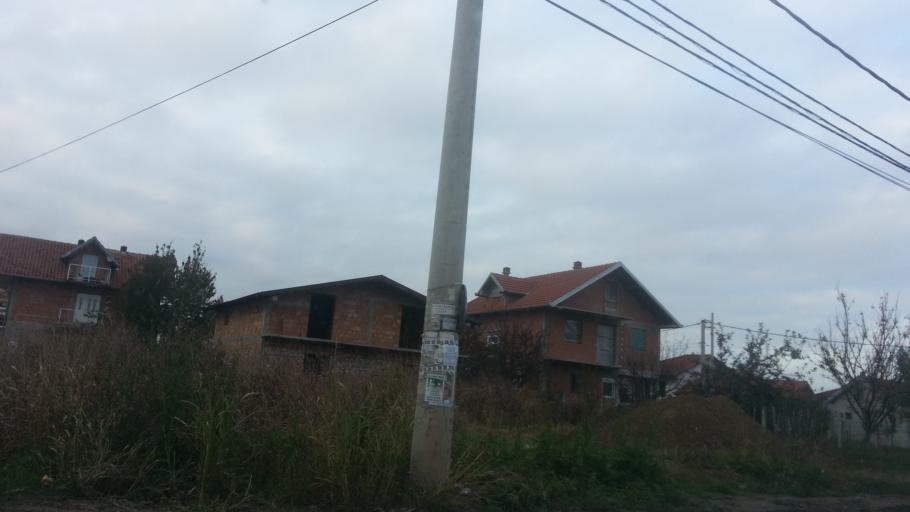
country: RS
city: Novi Banovci
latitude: 44.9174
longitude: 20.2749
